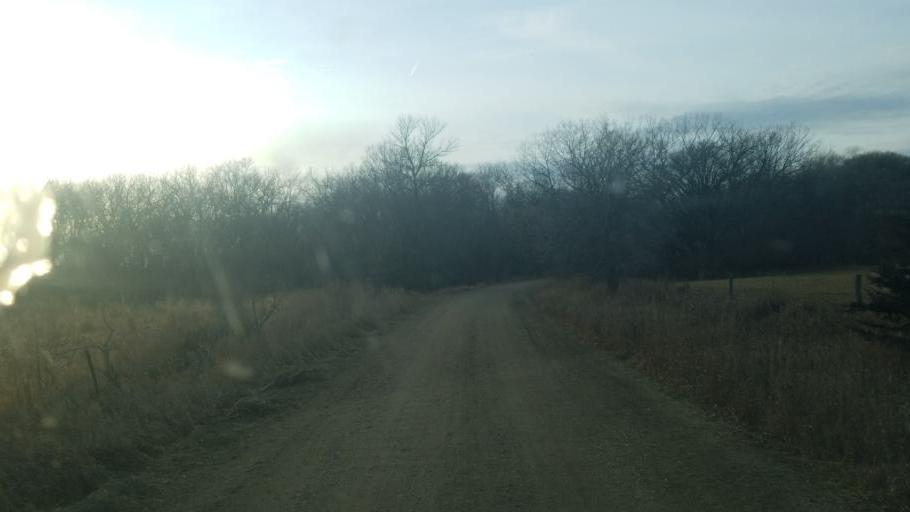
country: US
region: Nebraska
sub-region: Knox County
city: Center
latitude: 42.6801
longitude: -97.8144
